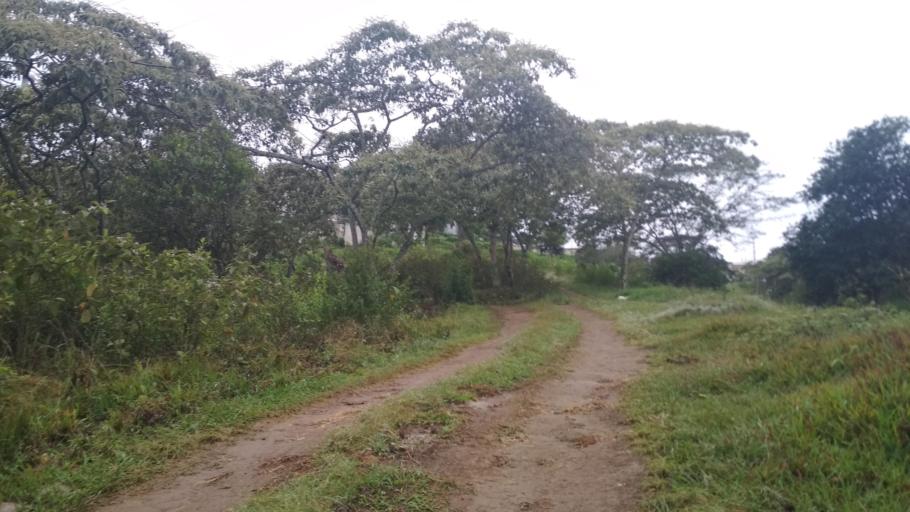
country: MX
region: Veracruz
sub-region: Emiliano Zapata
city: Las Trancas
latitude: 19.5067
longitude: -96.8694
